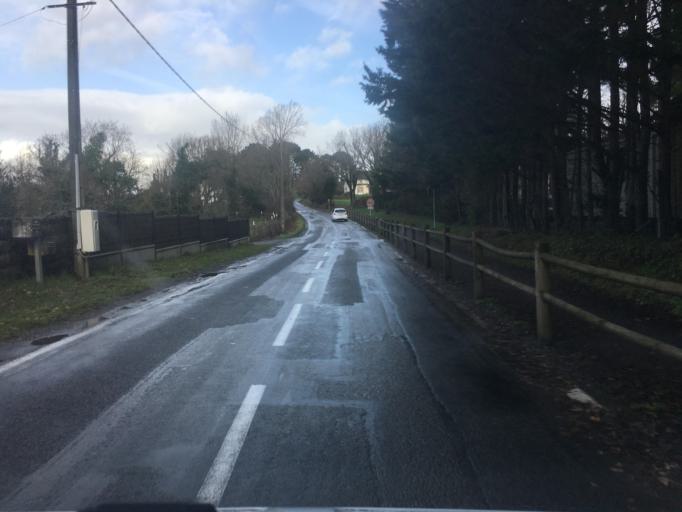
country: FR
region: Brittany
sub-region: Departement du Morbihan
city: Sarzeau
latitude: 47.5062
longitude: -2.7720
